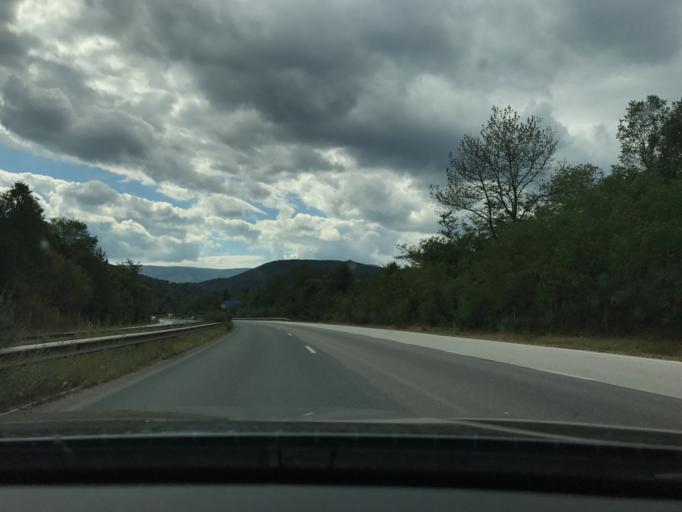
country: BG
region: Sofiya
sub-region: Obshtina Botevgrad
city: Botevgrad
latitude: 42.8903
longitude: 23.8203
